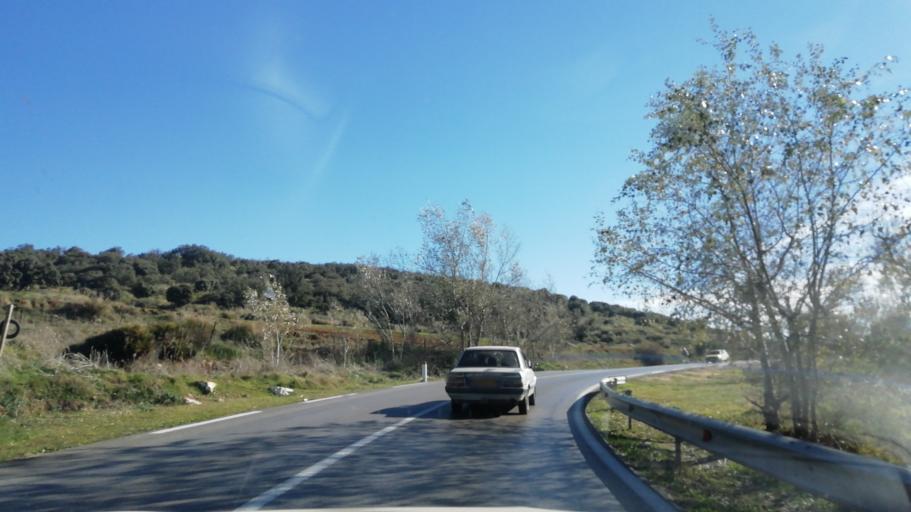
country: DZ
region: Tlemcen
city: Mansoura
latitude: 34.8325
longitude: -1.3714
